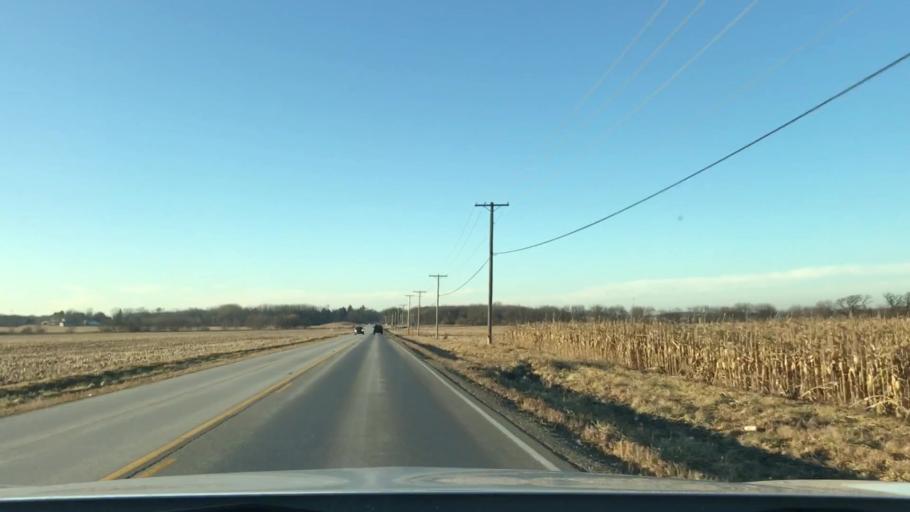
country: US
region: Illinois
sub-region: Kane County
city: Gilberts
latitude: 42.0841
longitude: -88.3873
